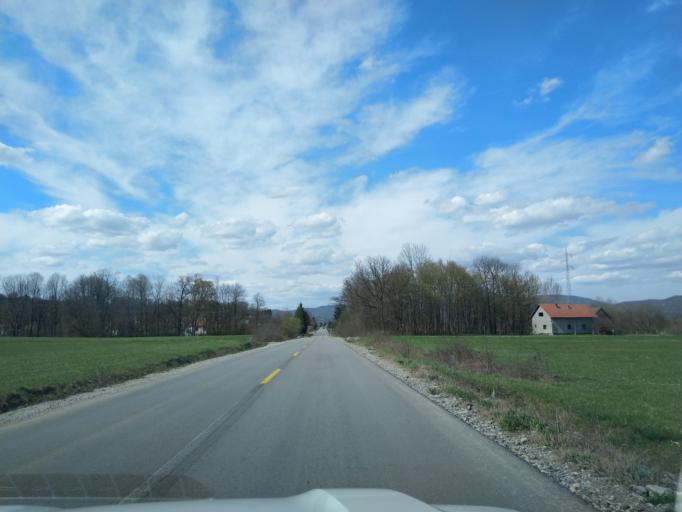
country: RS
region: Central Serbia
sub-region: Zlatiborski Okrug
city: Arilje
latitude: 43.8063
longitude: 20.0928
